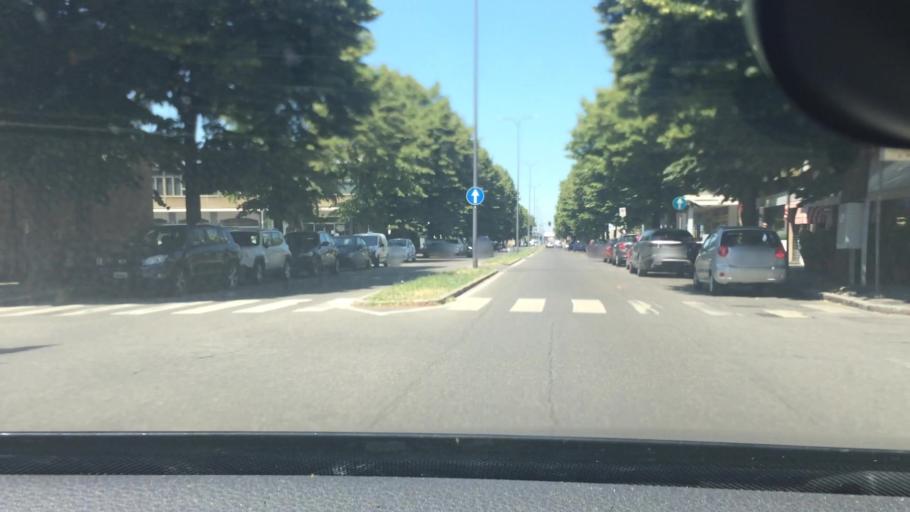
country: IT
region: Emilia-Romagna
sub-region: Provincia di Piacenza
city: Piacenza
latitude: 45.0455
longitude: 9.6717
